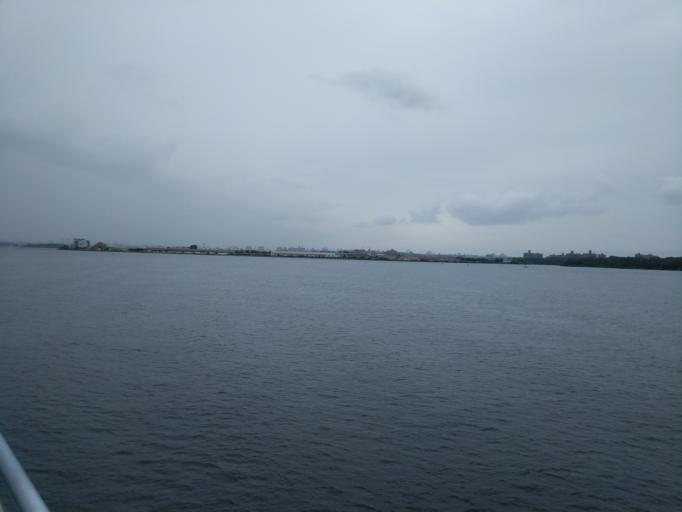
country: US
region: New York
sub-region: Bronx
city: The Bronx
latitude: 40.8011
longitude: -73.8575
